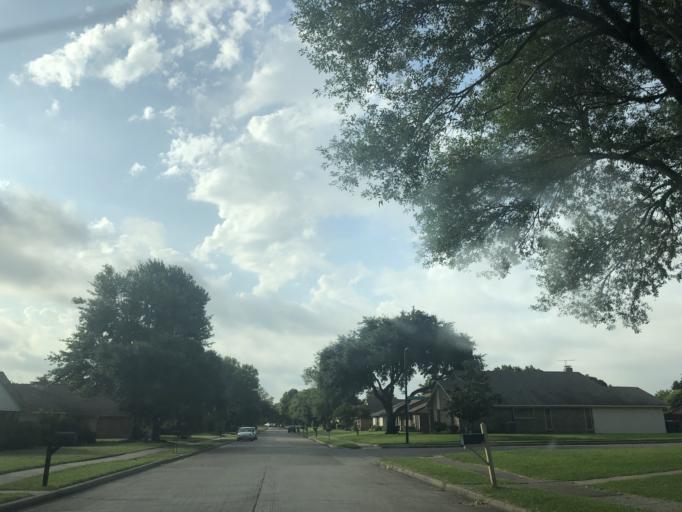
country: US
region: Texas
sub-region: Dallas County
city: Garland
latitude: 32.8520
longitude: -96.6309
